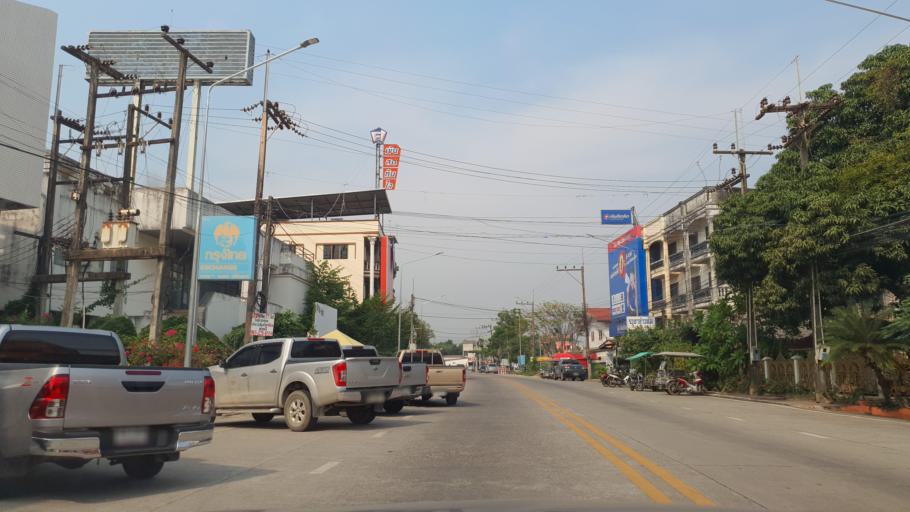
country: TH
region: Rayong
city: Rayong
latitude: 12.6255
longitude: 101.4334
